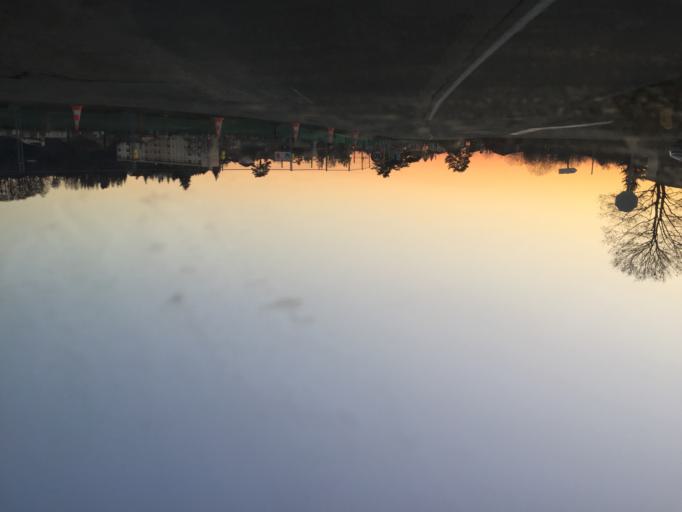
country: FR
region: Rhone-Alpes
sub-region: Departement de l'Ain
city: Beligneux
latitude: 45.8496
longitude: 5.1294
